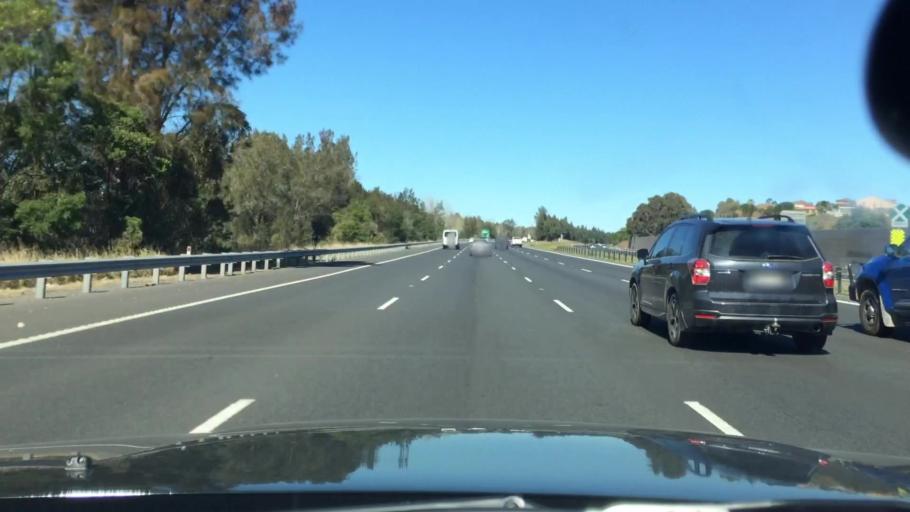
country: AU
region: New South Wales
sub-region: Campbelltown Municipality
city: Denham Court
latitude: -33.9940
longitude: 150.8503
